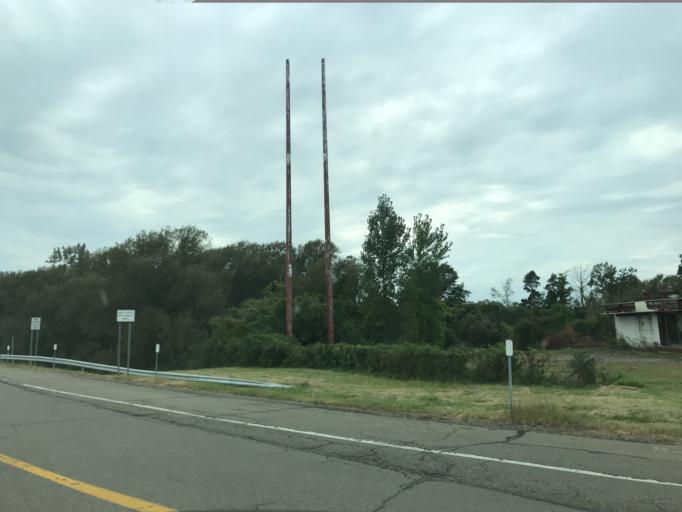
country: US
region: Pennsylvania
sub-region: Erie County
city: North East
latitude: 42.2633
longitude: -79.7462
